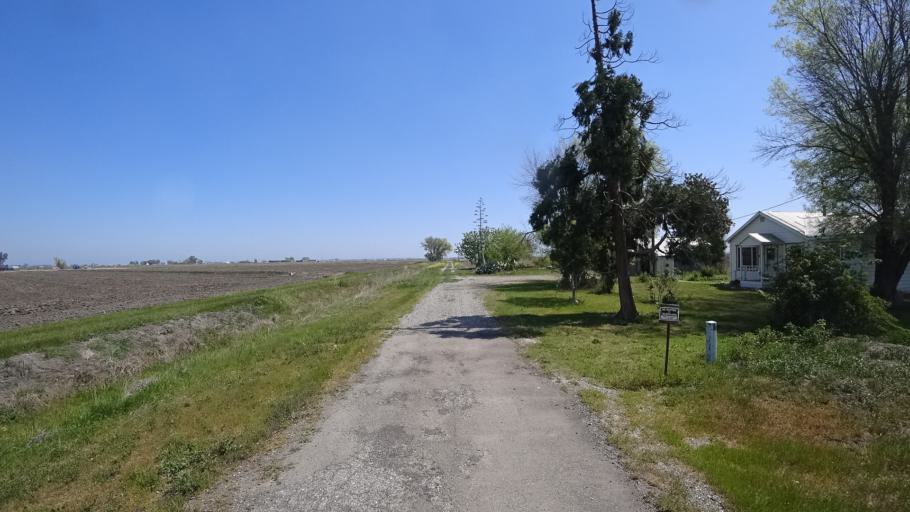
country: US
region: California
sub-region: Glenn County
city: Willows
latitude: 39.5509
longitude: -122.0957
